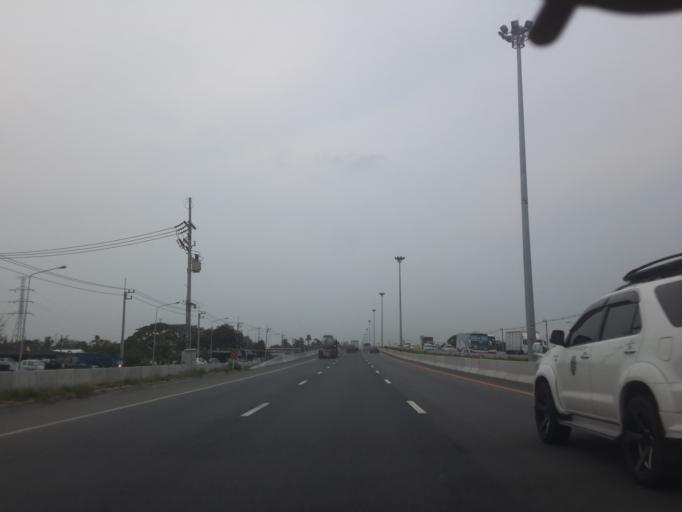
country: TH
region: Chon Buri
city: Ban Talat Bueng
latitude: 13.0743
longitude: 100.9939
